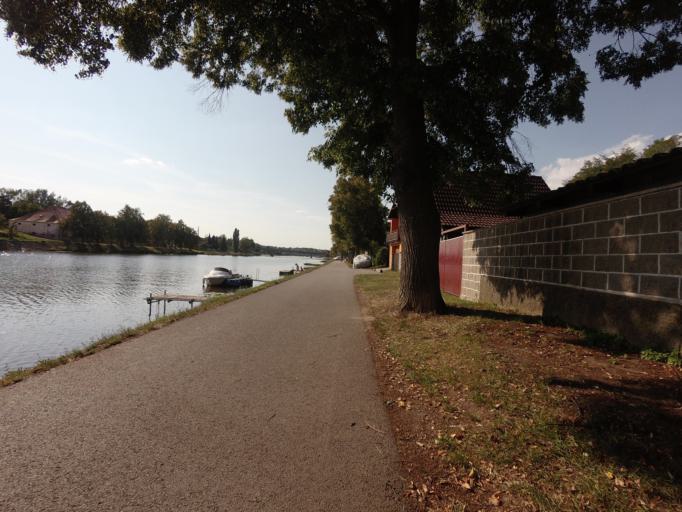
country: CZ
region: Jihocesky
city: Tyn nad Vltavou
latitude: 49.2194
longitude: 14.4266
